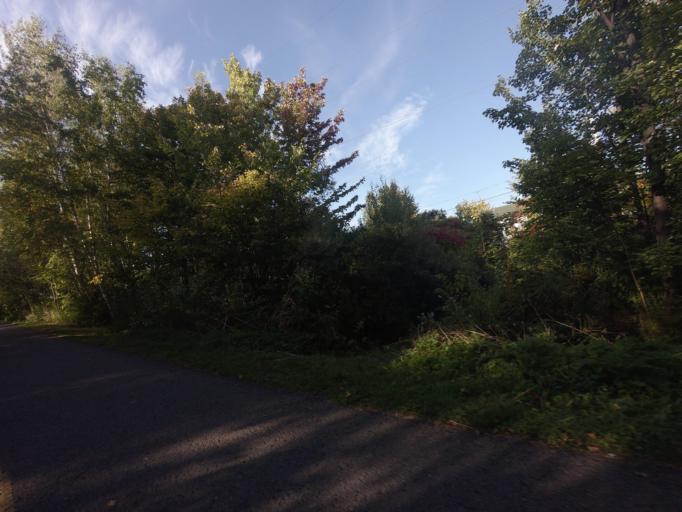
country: CA
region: Quebec
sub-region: Laurentides
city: Saint-Jerome
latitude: 45.7938
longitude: -73.9987
